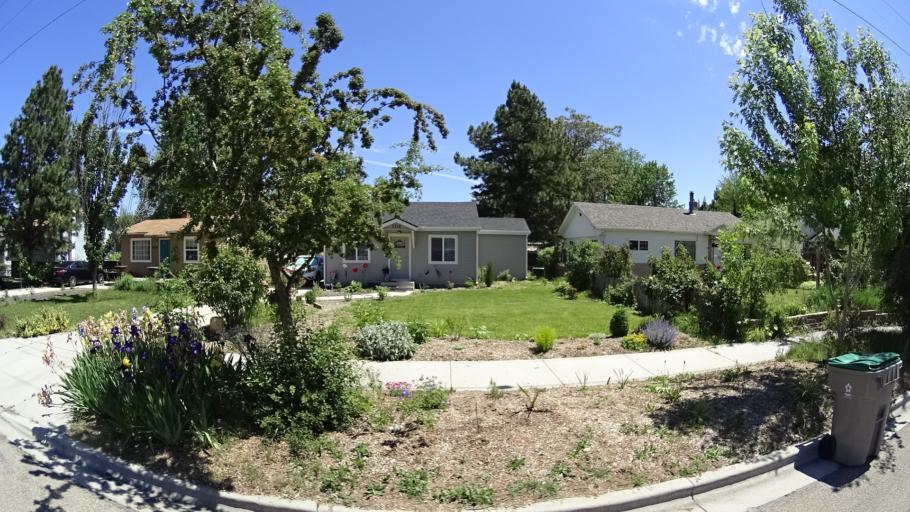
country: US
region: Idaho
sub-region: Ada County
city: Boise
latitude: 43.5842
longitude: -116.2286
